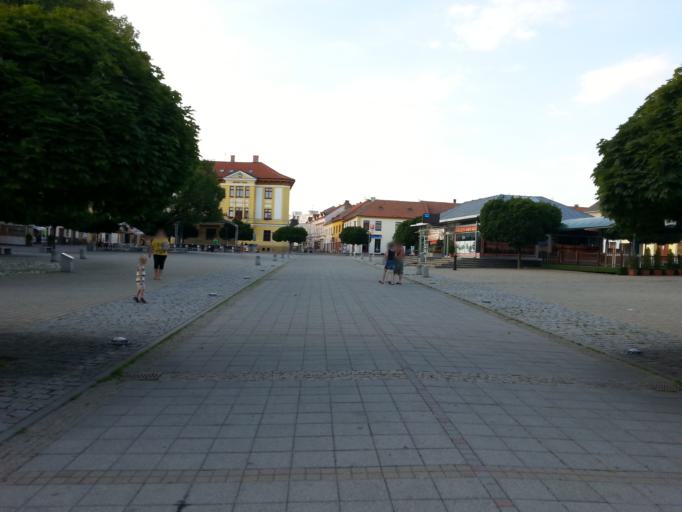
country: SK
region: Trenciansky
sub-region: Okres Nove Mesto nad Vahom
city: Nove Mesto nad Vahom
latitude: 48.7576
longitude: 17.8309
